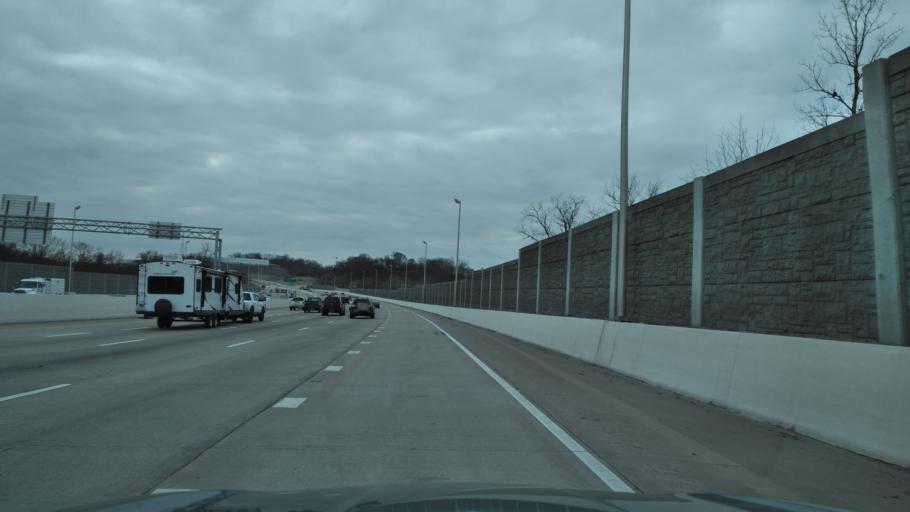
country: US
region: Tennessee
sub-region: Davidson County
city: Nashville
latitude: 36.2333
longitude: -86.7685
